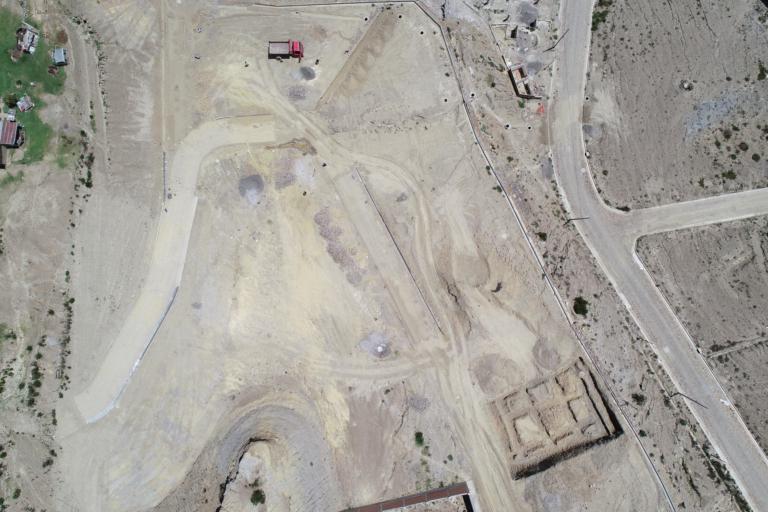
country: BO
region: La Paz
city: La Paz
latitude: -16.5237
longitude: -68.0496
